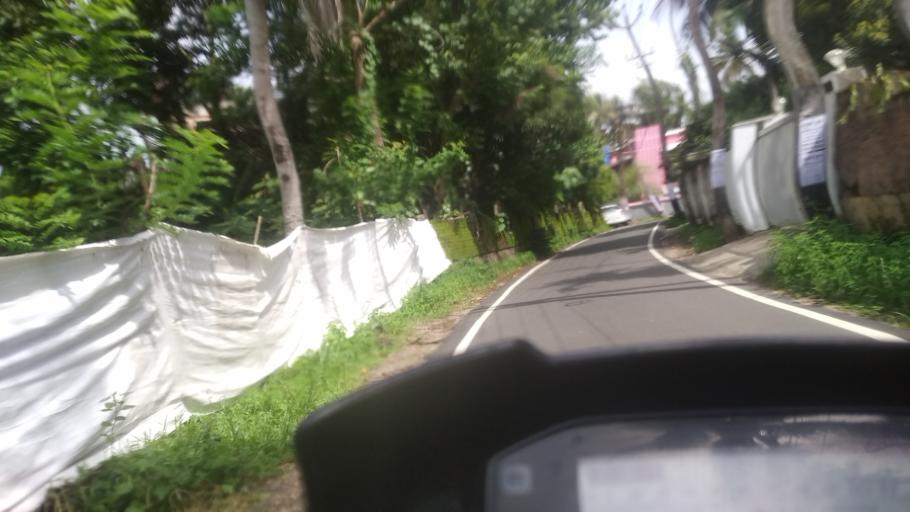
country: IN
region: Kerala
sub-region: Ernakulam
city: Elur
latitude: 10.1417
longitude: 76.2378
